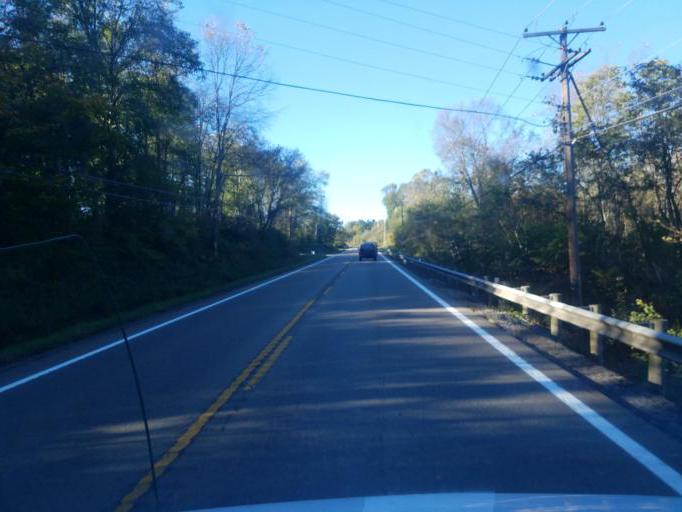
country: US
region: Ohio
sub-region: Columbiana County
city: New Waterford
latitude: 40.7993
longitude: -80.6310
